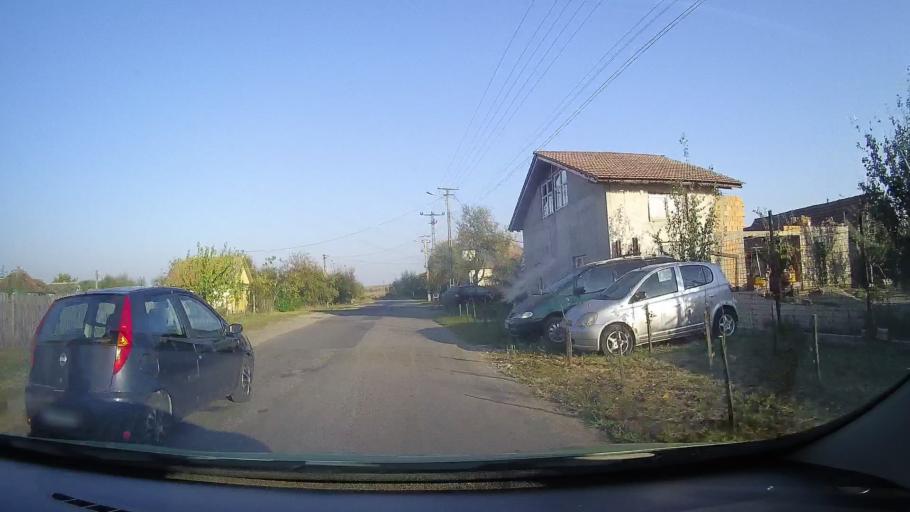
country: RO
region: Arad
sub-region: Comuna Tarnova
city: Tarnova
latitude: 46.3183
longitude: 21.8024
